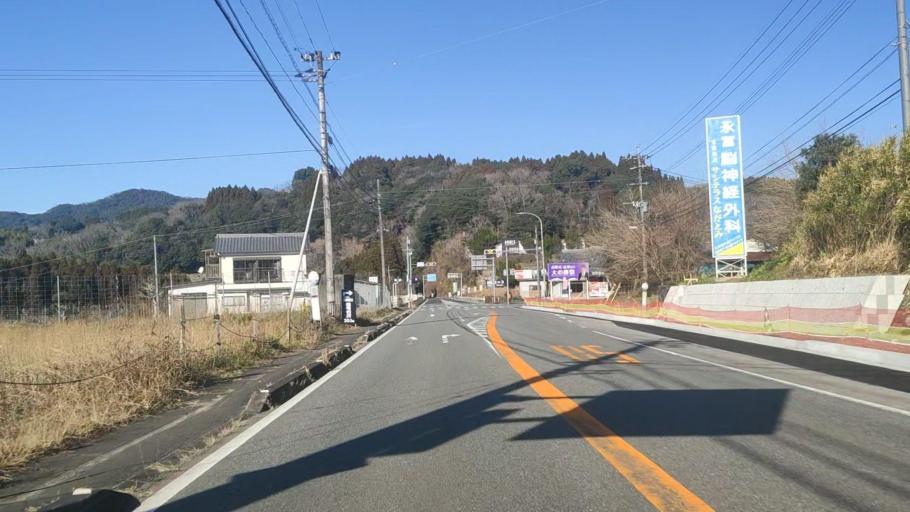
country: JP
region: Oita
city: Usuki
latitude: 33.0516
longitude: 131.6890
